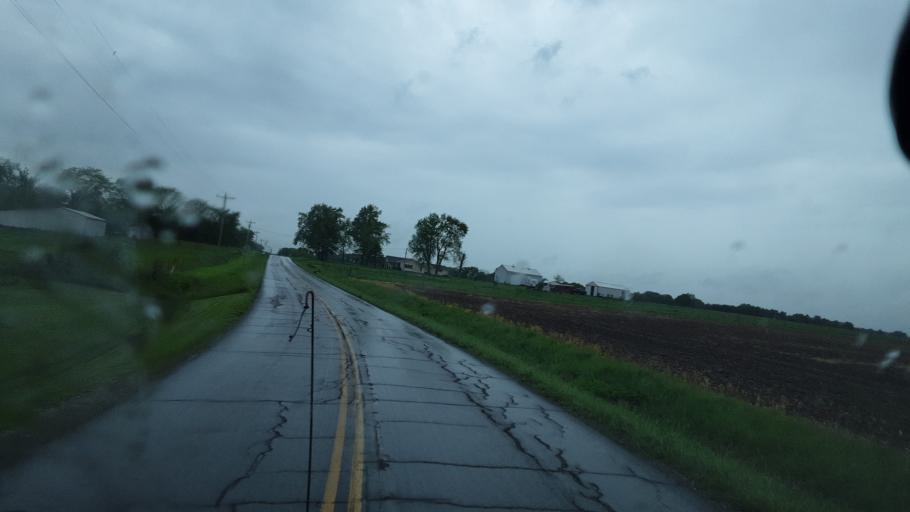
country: US
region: Missouri
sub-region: Randolph County
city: Moberly
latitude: 39.3926
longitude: -92.2356
